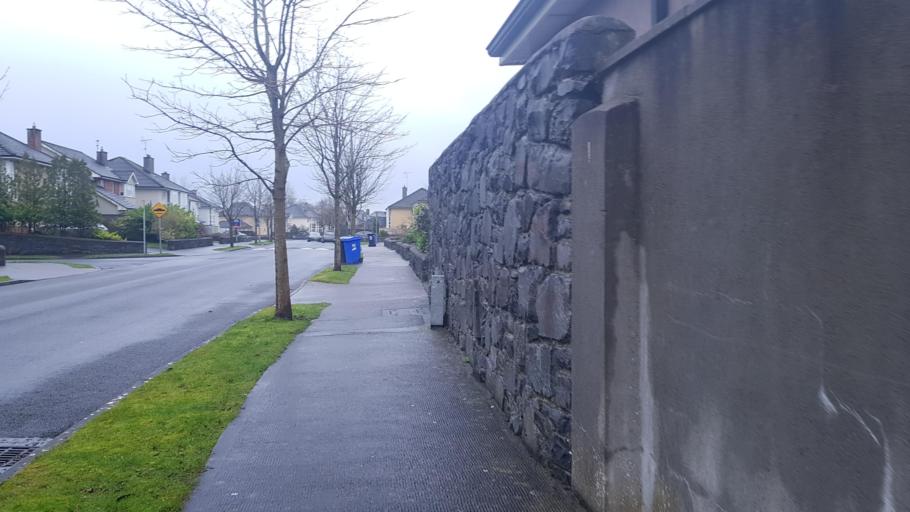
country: IE
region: Connaught
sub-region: County Galway
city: Tuam
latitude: 53.5240
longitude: -8.8474
